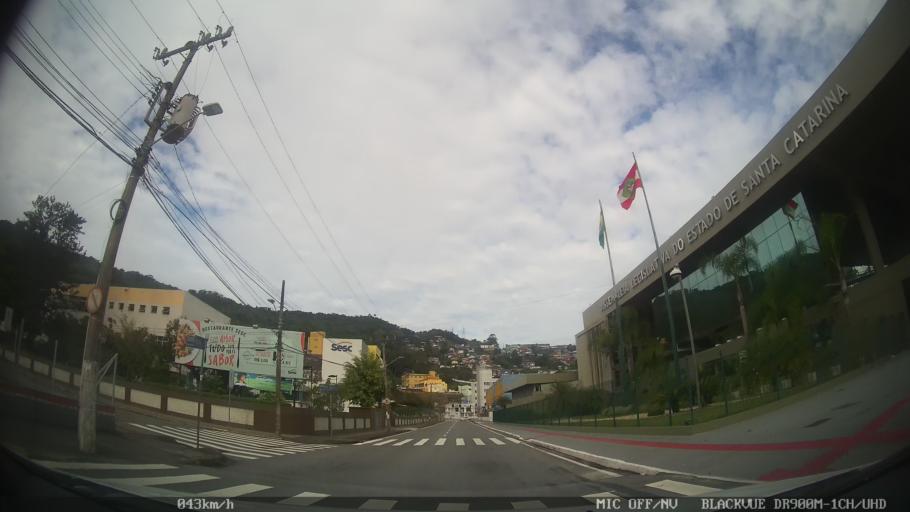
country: BR
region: Santa Catarina
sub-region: Florianopolis
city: Florianopolis
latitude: -27.6028
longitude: -48.5473
